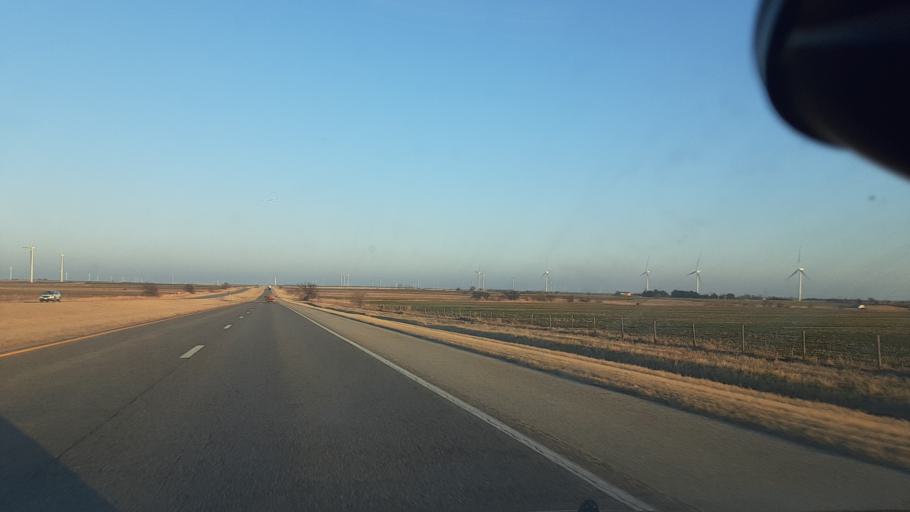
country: US
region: Oklahoma
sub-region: Noble County
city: Perry
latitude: 36.3975
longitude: -97.5091
